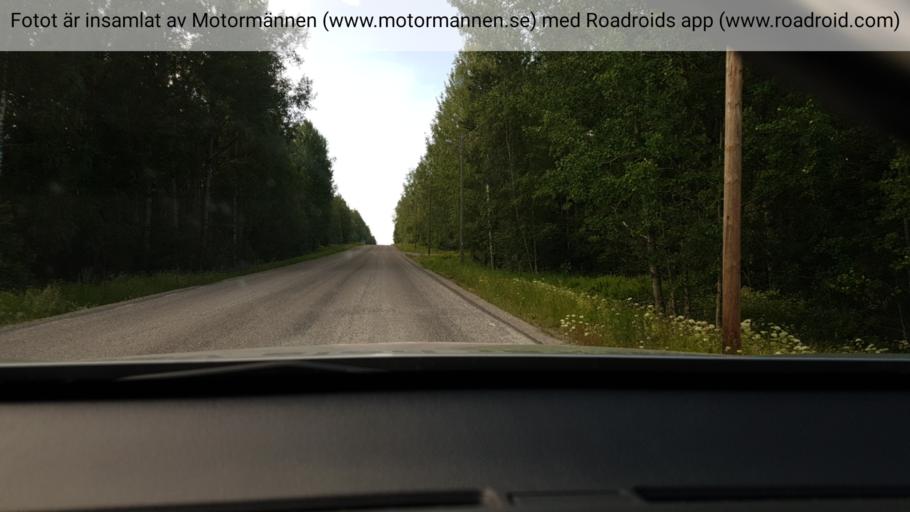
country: SE
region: Vaermland
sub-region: Filipstads Kommun
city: Filipstad
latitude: 59.8304
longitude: 14.1015
